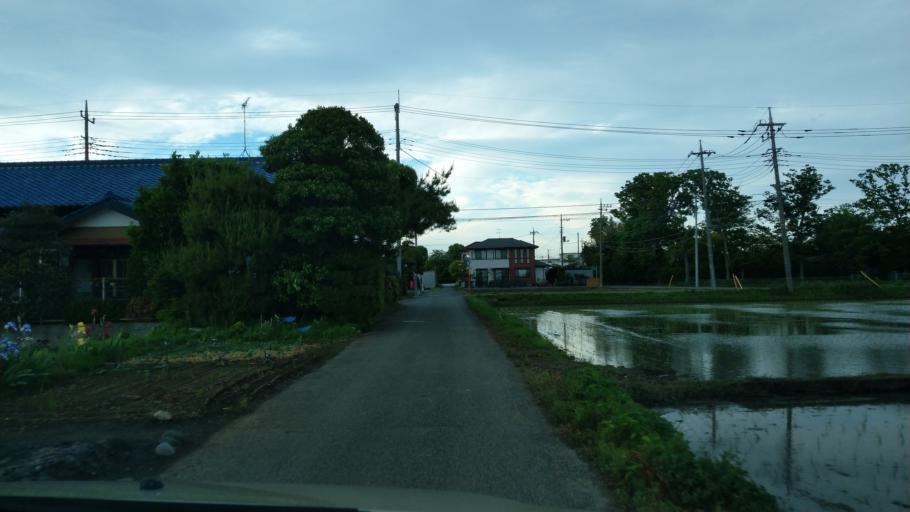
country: JP
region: Saitama
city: Yono
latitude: 35.8821
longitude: 139.5929
